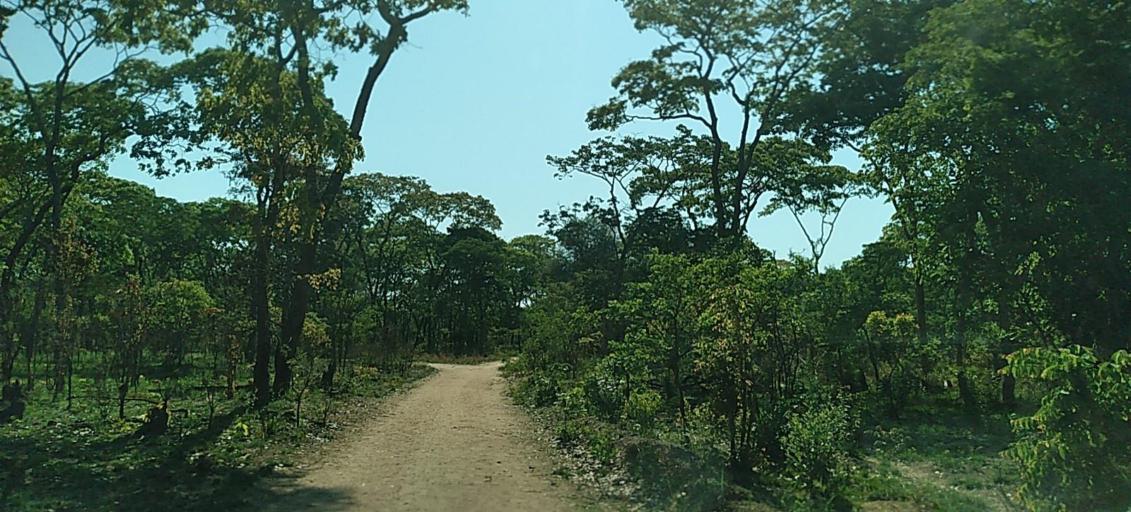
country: ZM
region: Central
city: Mkushi
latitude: -13.4703
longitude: 28.9737
